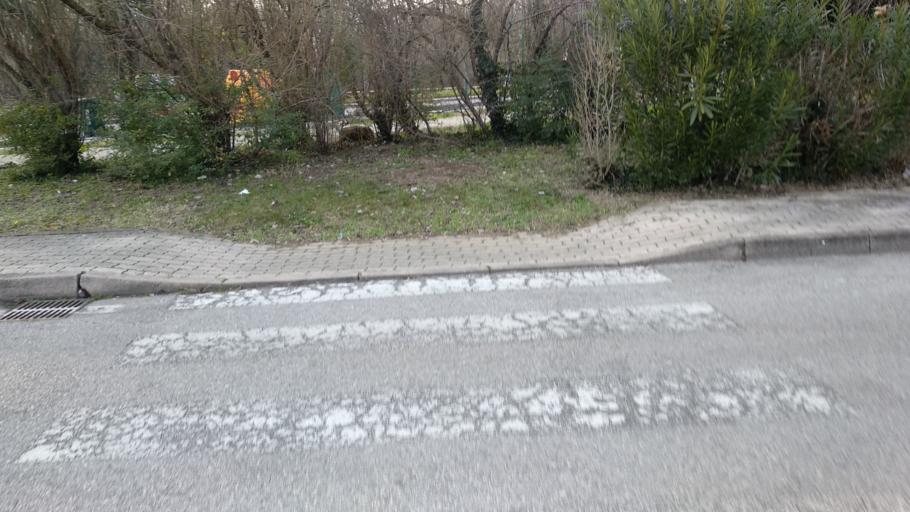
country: IT
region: Veneto
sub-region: Provincia di Venezia
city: Campalto
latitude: 45.4826
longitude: 12.2684
